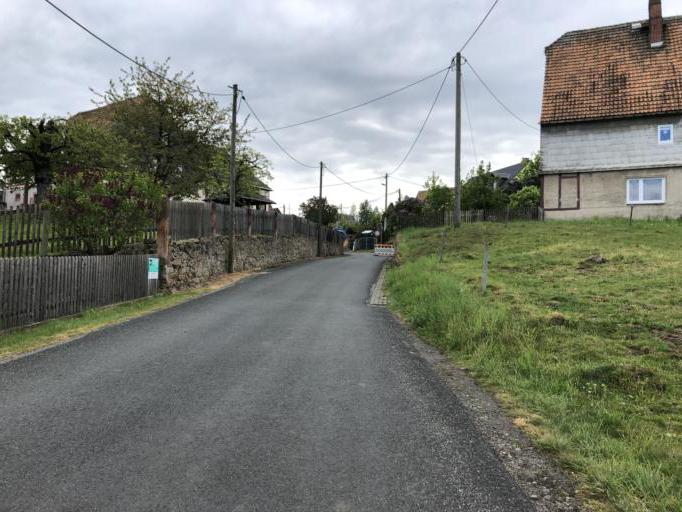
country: DE
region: Saxony
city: Wechselburg
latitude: 51.0204
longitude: 12.7887
